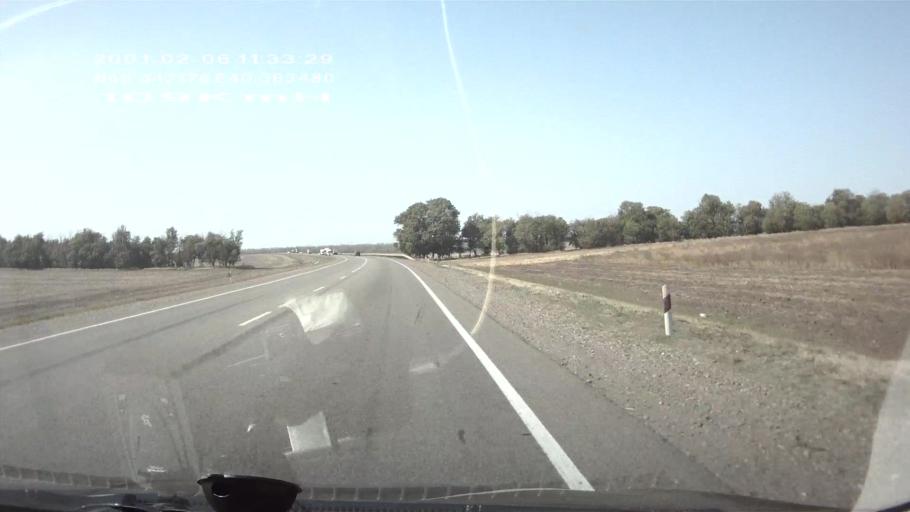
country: RU
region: Krasnodarskiy
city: Kazanskaya
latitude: 45.4463
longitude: 40.3612
